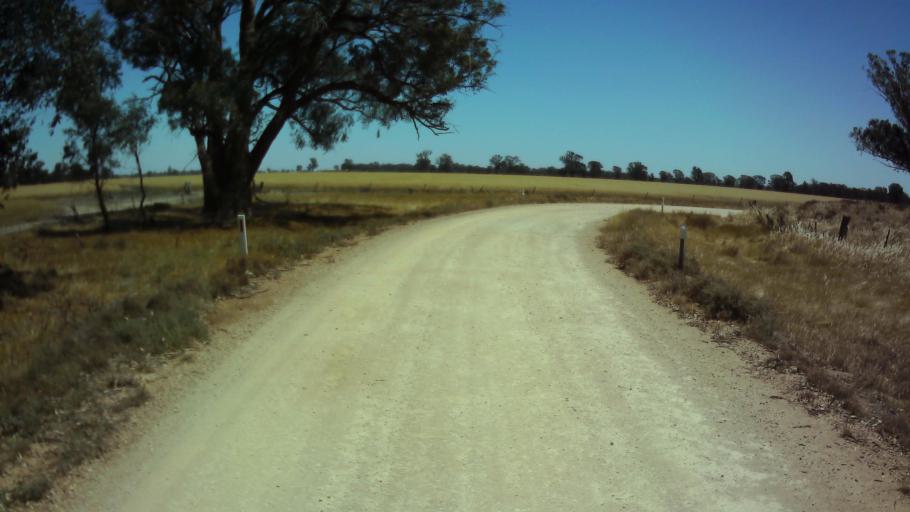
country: AU
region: New South Wales
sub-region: Weddin
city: Grenfell
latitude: -34.0073
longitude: 147.9563
